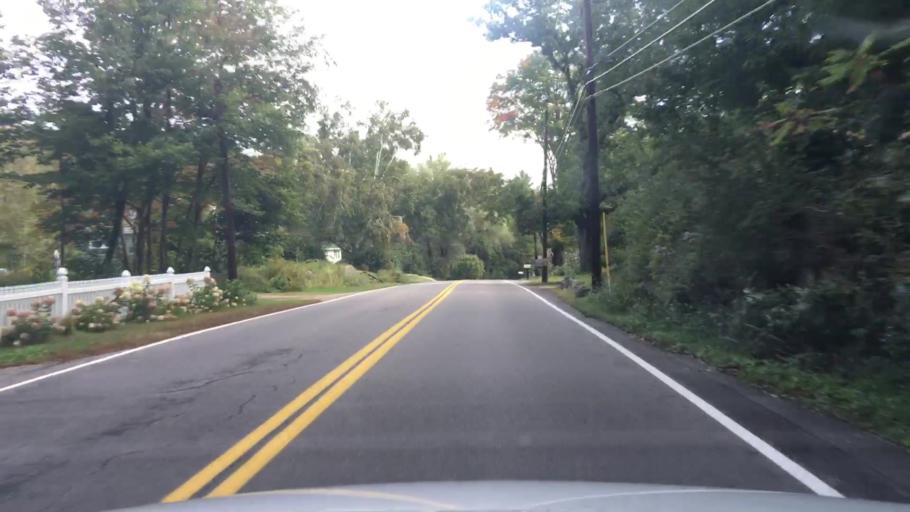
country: US
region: Maine
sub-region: York County
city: Kittery Point
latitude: 43.0904
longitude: -70.6809
